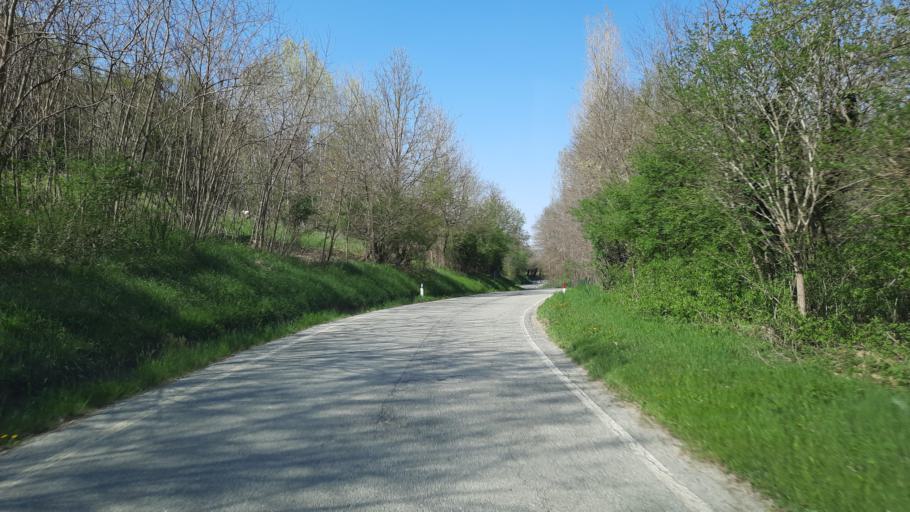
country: IT
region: Piedmont
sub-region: Provincia di Alessandria
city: Moncestino
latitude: 45.1464
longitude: 8.1281
